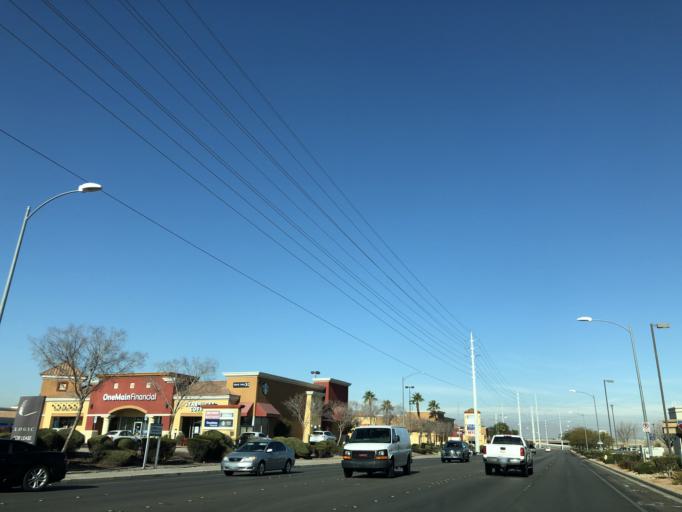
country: US
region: Nevada
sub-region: Clark County
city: Whitney
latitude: 36.0654
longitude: -115.0362
